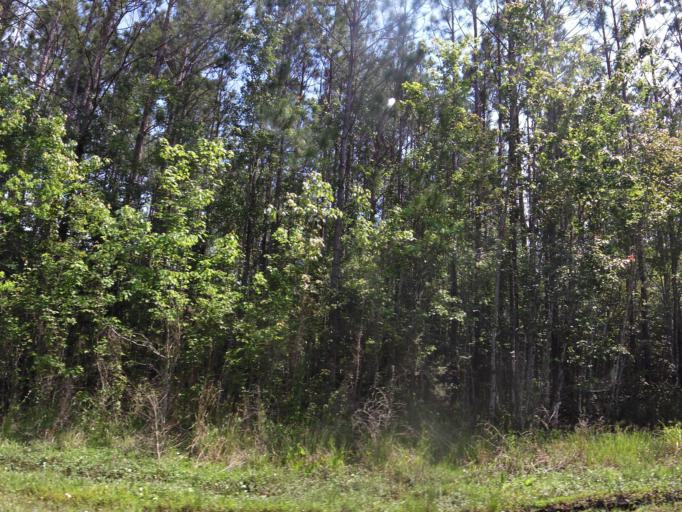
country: US
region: Florida
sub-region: Nassau County
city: Nassau Village-Ratliff
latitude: 30.4968
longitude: -81.6681
